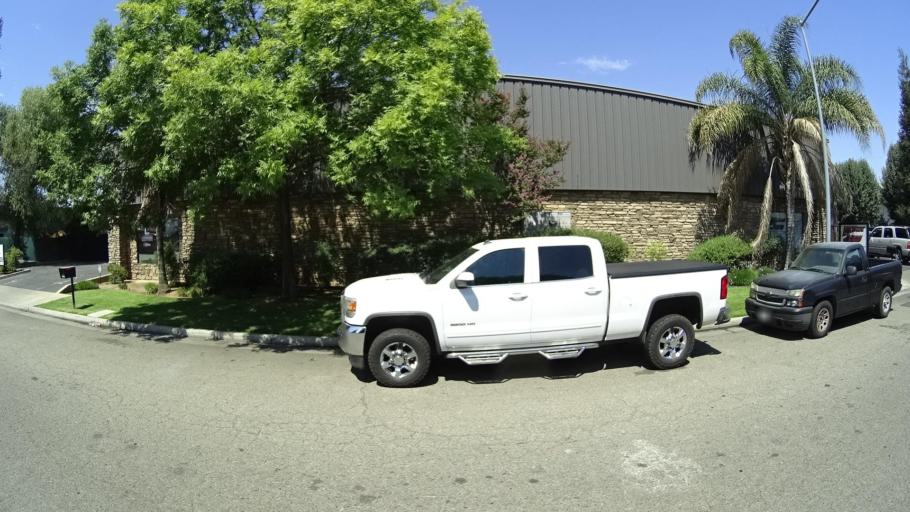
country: US
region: California
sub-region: Fresno County
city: Tarpey Village
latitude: 36.7729
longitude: -119.6857
